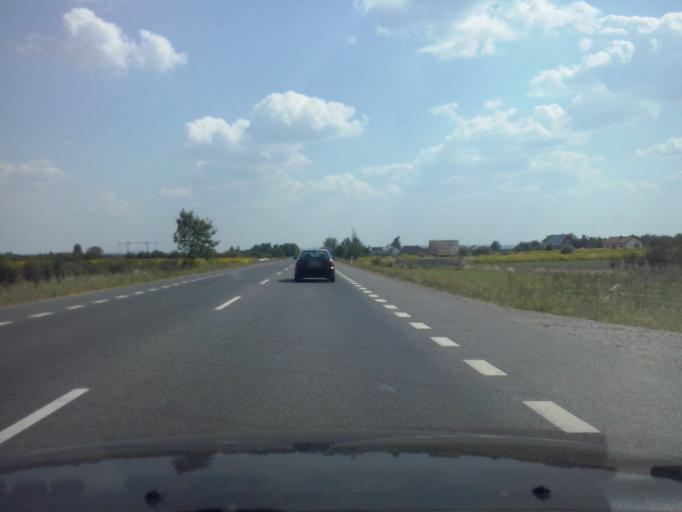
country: PL
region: Swietokrzyskie
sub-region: Powiat sandomierski
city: Loniow
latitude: 50.5525
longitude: 21.5386
